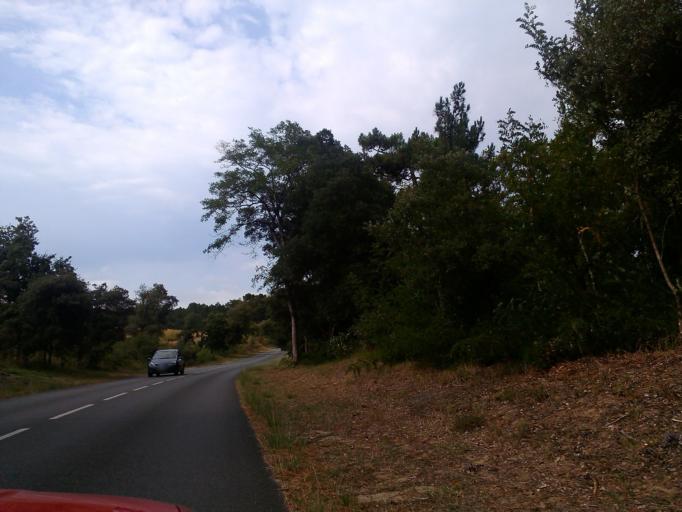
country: FR
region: Poitou-Charentes
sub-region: Departement de la Charente-Maritime
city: La Tremblade
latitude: 45.7901
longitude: -1.1842
